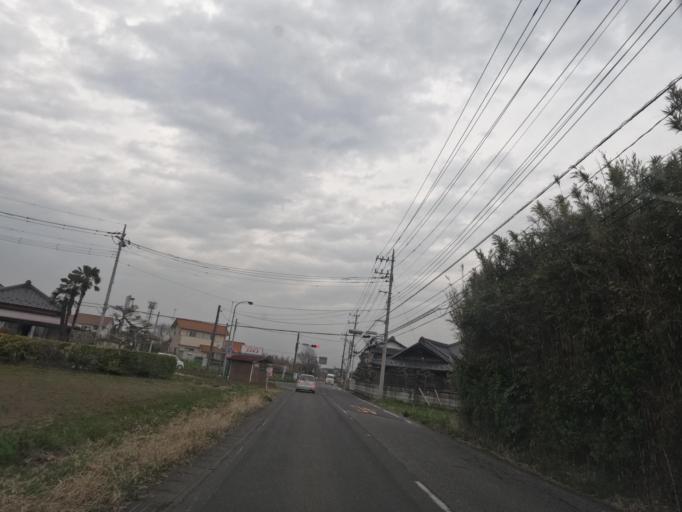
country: JP
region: Ibaraki
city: Toride
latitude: 35.9319
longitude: 140.0606
